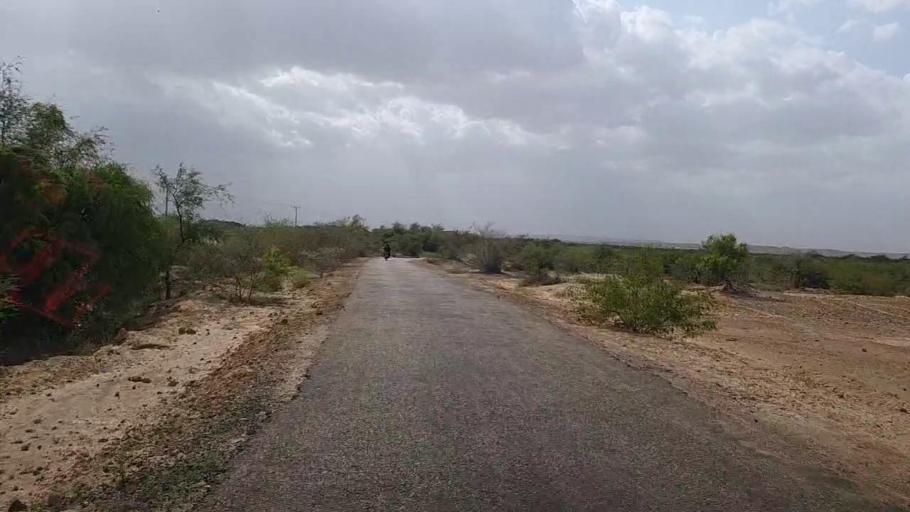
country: PK
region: Sindh
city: Jamshoro
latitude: 25.3978
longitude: 67.7178
